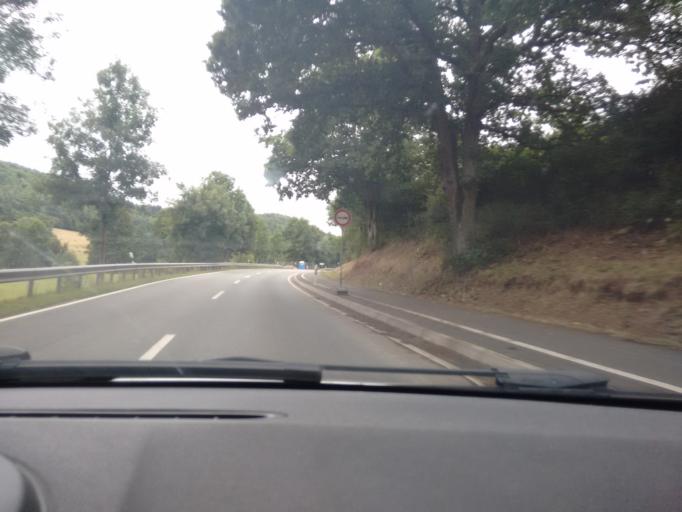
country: DE
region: Rheinland-Pfalz
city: Niederbrombach
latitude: 49.6832
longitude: 7.2359
